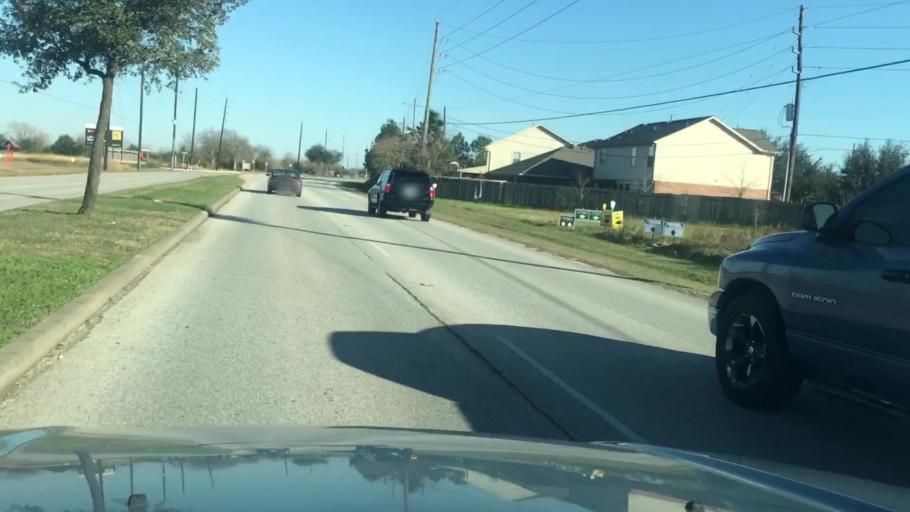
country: US
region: Texas
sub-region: Fort Bend County
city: Cinco Ranch
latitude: 29.8318
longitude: -95.7417
